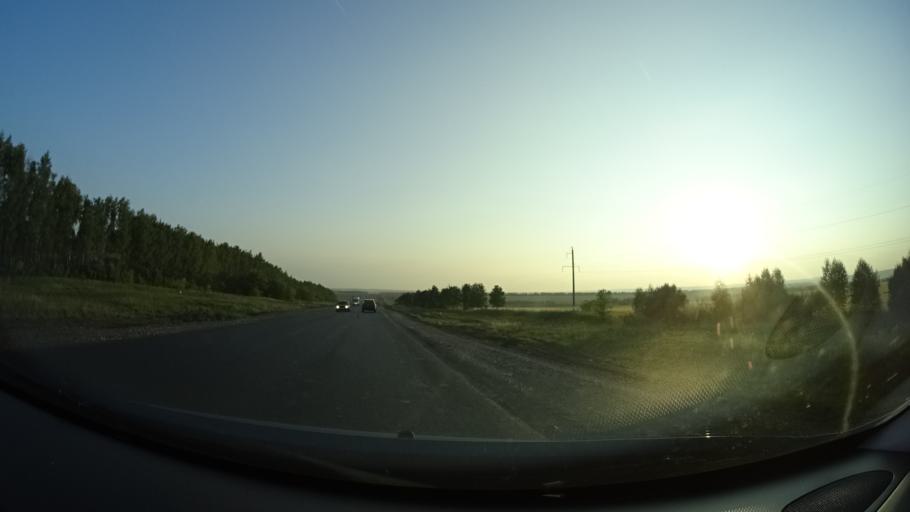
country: RU
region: Samara
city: Sernovodsk
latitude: 53.9683
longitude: 51.4395
